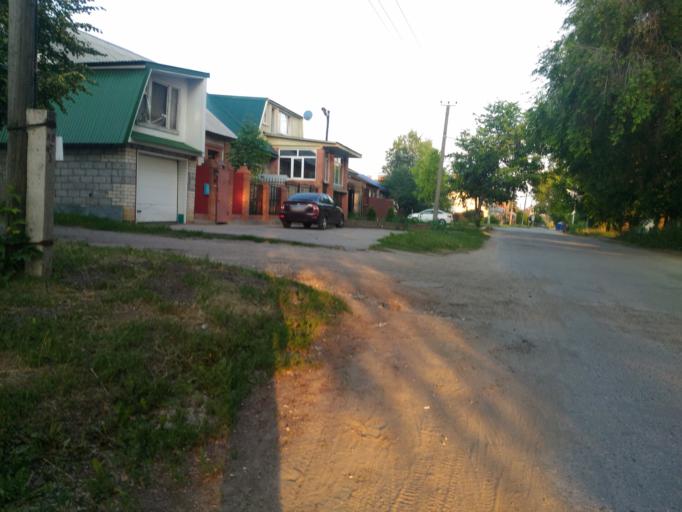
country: RU
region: Ulyanovsk
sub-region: Ulyanovskiy Rayon
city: Ulyanovsk
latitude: 54.3393
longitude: 48.3689
